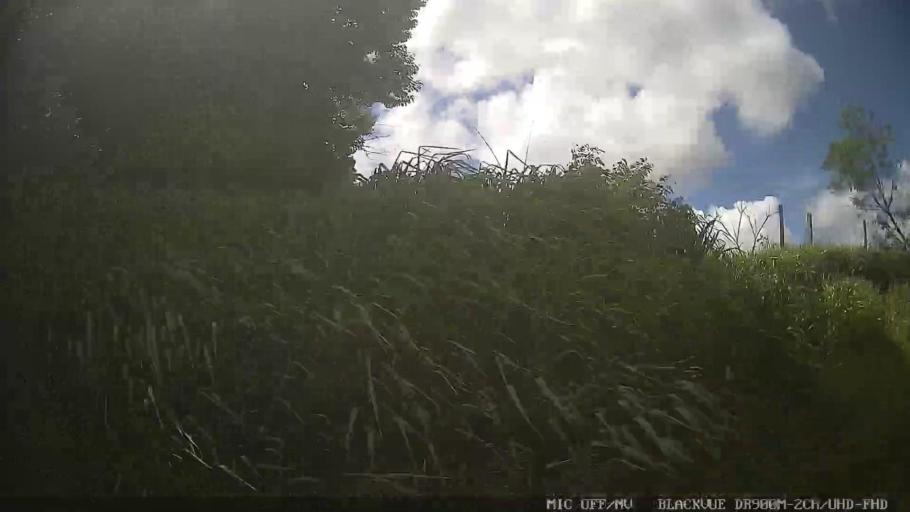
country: BR
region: Sao Paulo
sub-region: Amparo
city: Amparo
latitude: -22.8438
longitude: -46.7138
